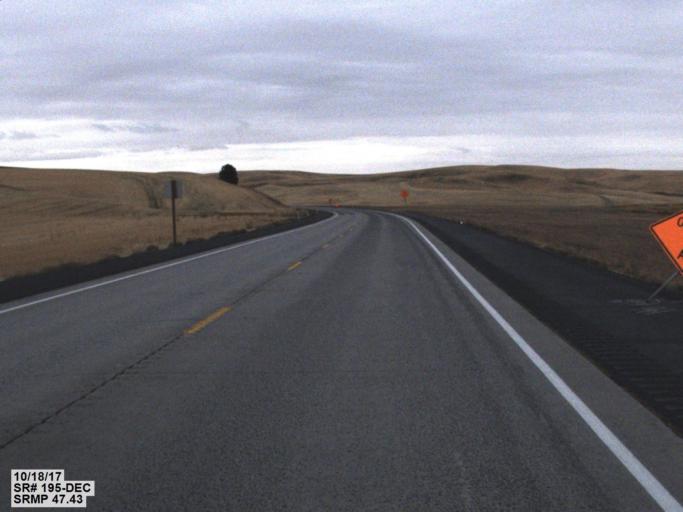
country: US
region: Washington
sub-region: Whitman County
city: Colfax
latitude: 46.9978
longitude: -117.3540
